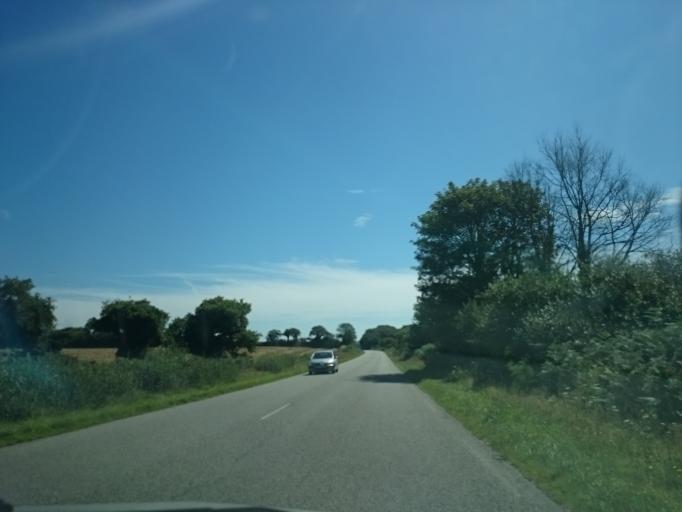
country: FR
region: Brittany
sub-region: Departement du Finistere
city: Lanrivoare
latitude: 48.4363
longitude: -4.6670
